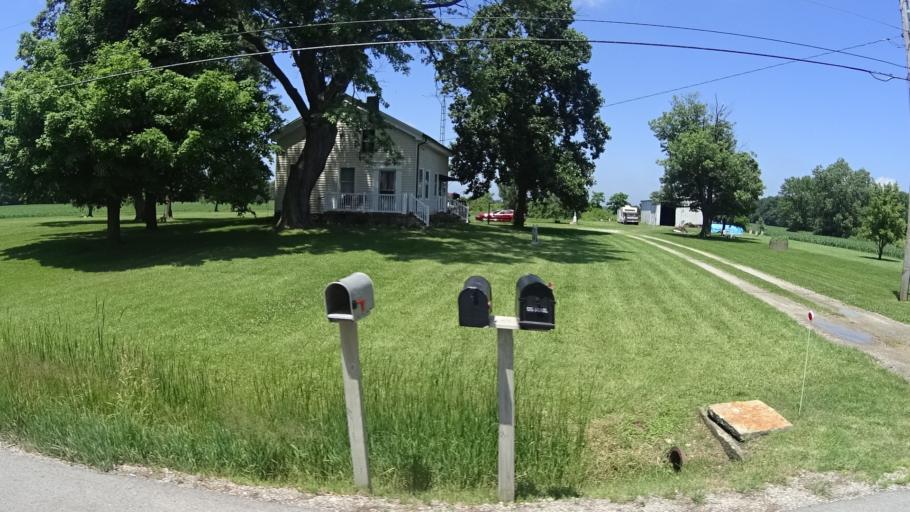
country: US
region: Ohio
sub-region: Huron County
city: Wakeman
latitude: 41.3274
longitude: -82.3835
